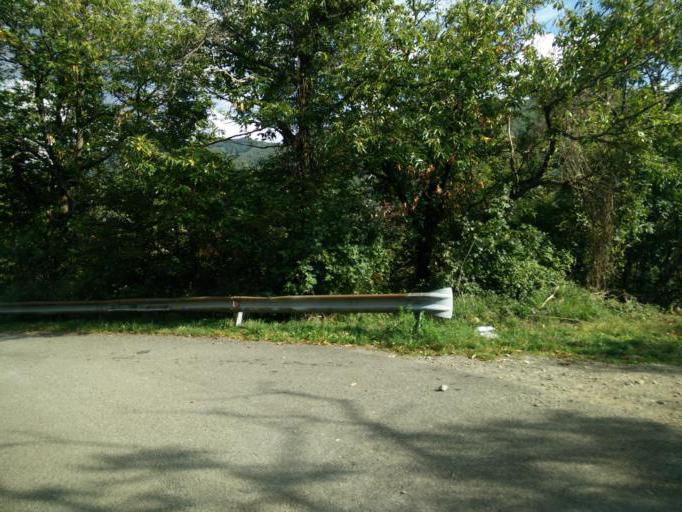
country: IT
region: Tuscany
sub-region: Provincia di Massa-Carrara
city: Zeri
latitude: 44.3499
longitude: 9.7864
